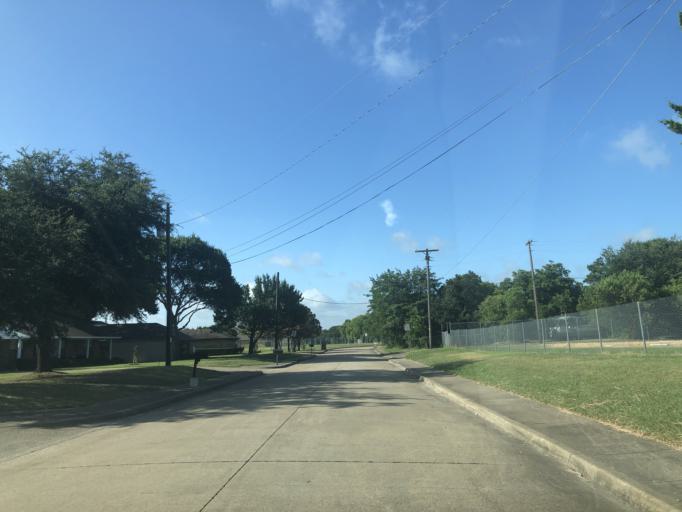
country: US
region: Texas
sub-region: Dallas County
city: Duncanville
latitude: 32.6582
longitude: -96.9276
